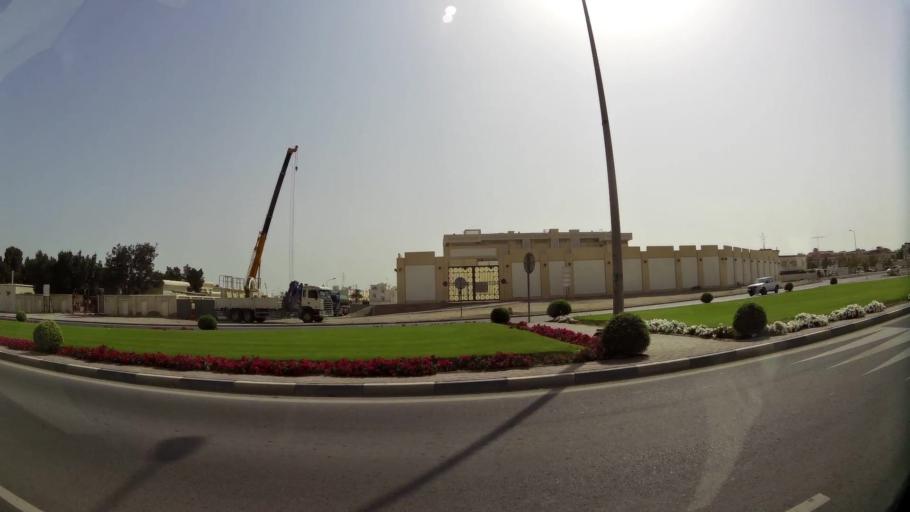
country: QA
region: Baladiyat ad Dawhah
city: Doha
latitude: 25.2469
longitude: 51.5241
